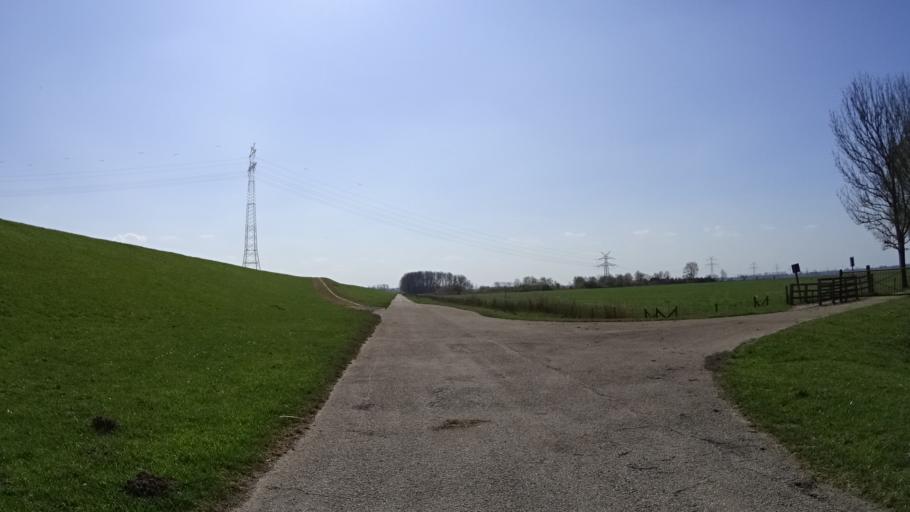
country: DE
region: Lower Saxony
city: Weener
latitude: 53.1513
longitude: 7.3709
